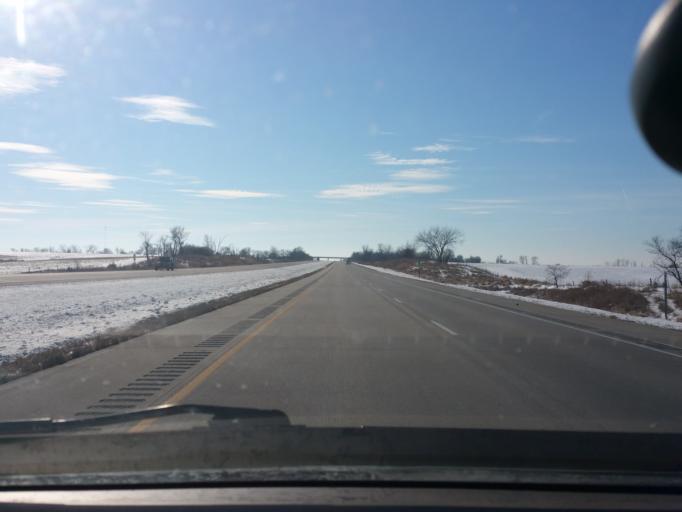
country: US
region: Iowa
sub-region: Clarke County
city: Osceola
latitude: 40.9536
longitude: -93.7992
